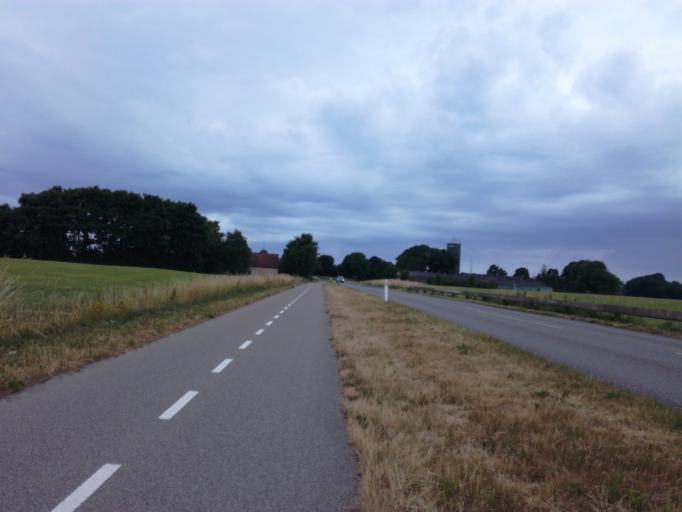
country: DK
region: South Denmark
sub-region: Vejle Kommune
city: Borkop
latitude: 55.6563
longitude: 9.6369
